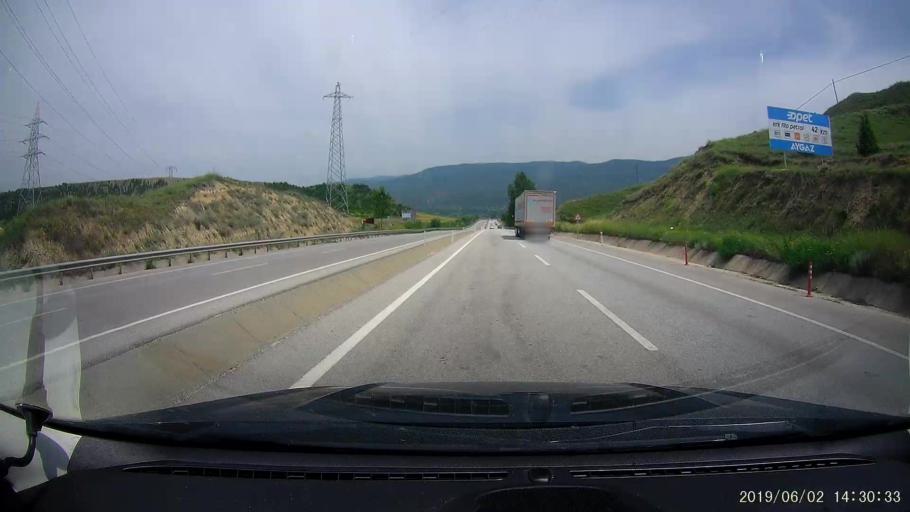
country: TR
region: Kastamonu
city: Tosya
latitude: 41.0171
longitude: 34.1175
